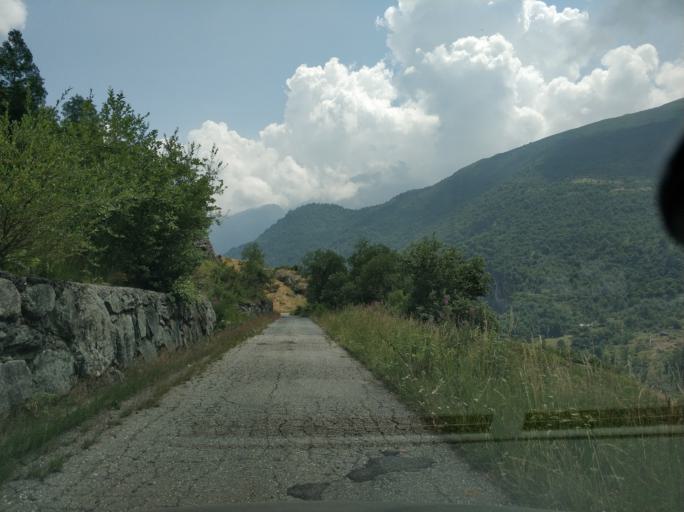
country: IT
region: Piedmont
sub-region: Provincia di Torino
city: Usseglio
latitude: 45.2474
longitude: 7.1777
